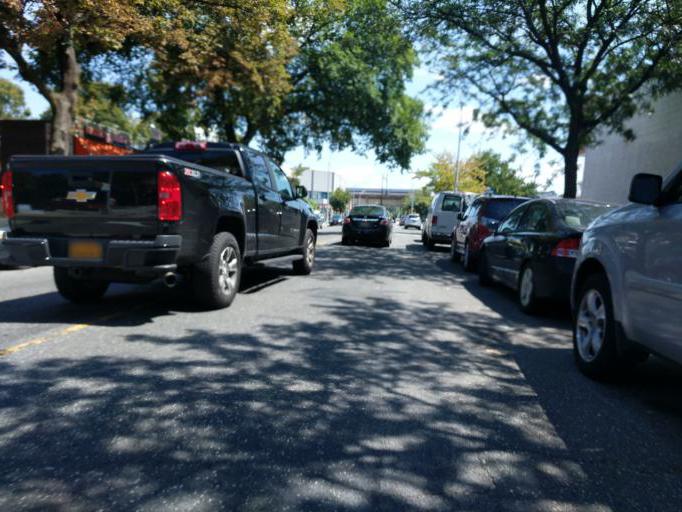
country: US
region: New York
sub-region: Queens County
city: Long Island City
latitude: 40.7542
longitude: -73.9089
